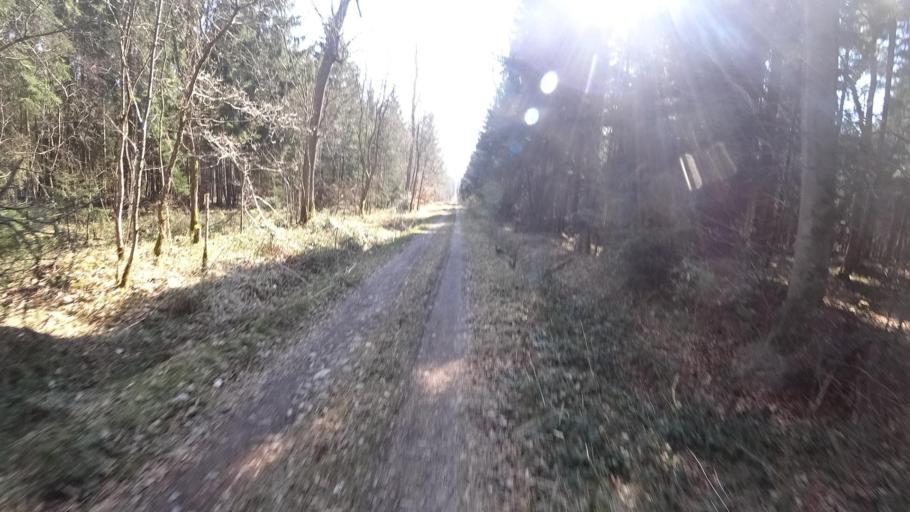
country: DE
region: Rheinland-Pfalz
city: Steinbach
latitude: 50.0314
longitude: 7.6100
